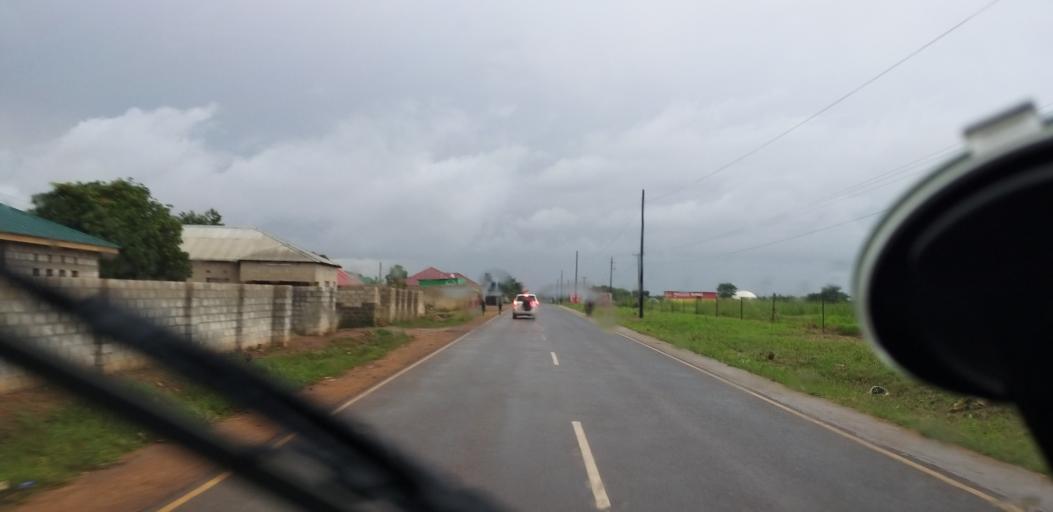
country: ZM
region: Lusaka
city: Lusaka
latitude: -15.5050
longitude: 28.3120
